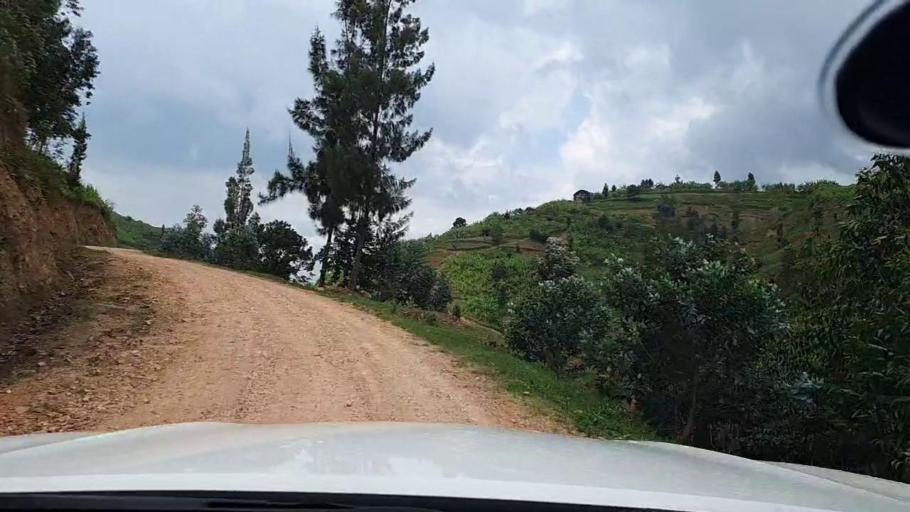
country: RW
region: Western Province
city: Kibuye
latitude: -2.1245
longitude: 29.4267
